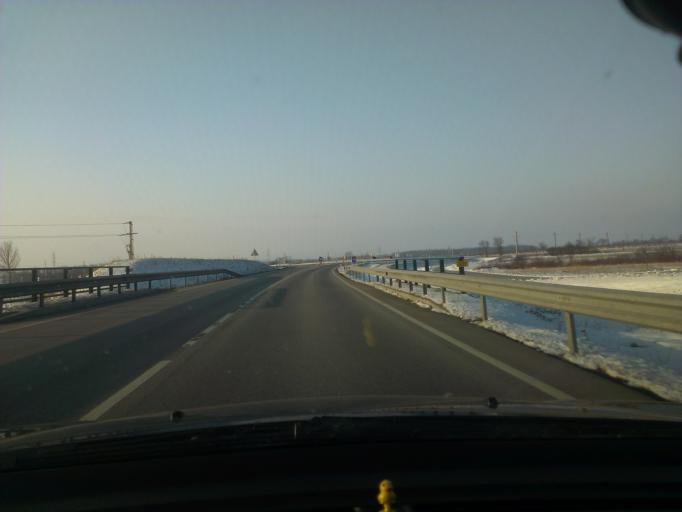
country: AT
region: Burgenland
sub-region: Eisenstadt-Umgebung
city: Schutzen am Gebirge
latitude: 47.8482
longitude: 16.6033
